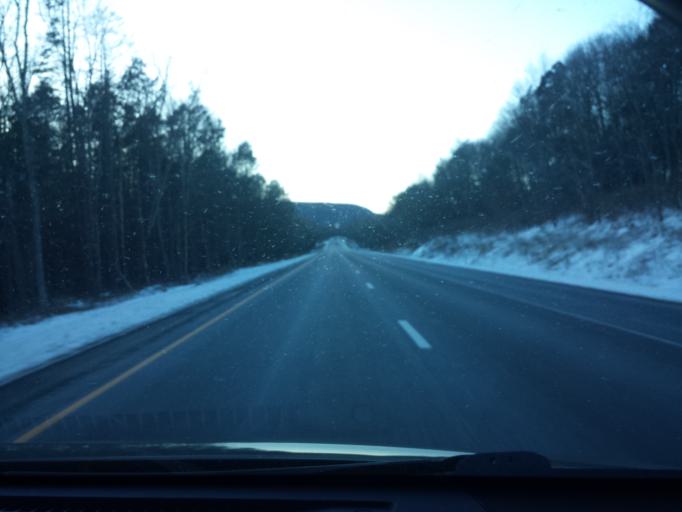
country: US
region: Pennsylvania
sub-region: Clinton County
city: Castanea
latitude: 41.0485
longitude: -77.3249
